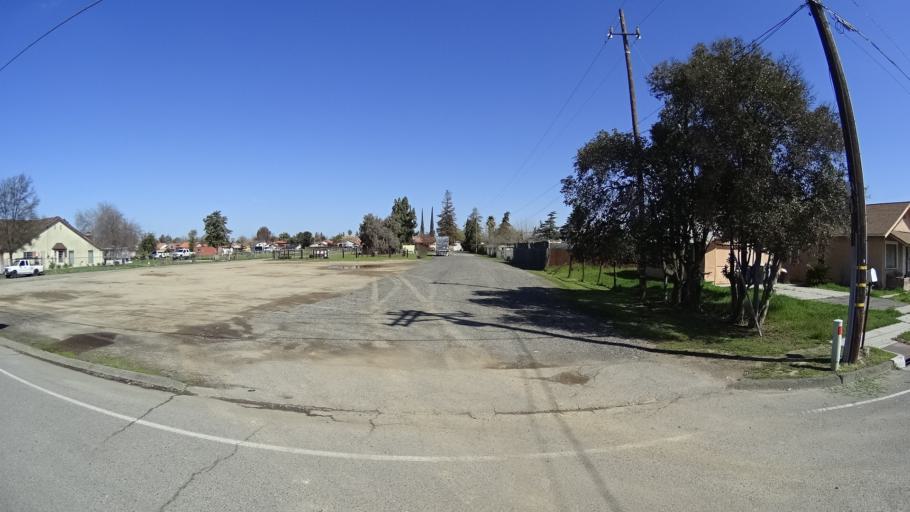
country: US
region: California
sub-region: Fresno County
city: West Park
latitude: 36.7646
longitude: -119.8758
